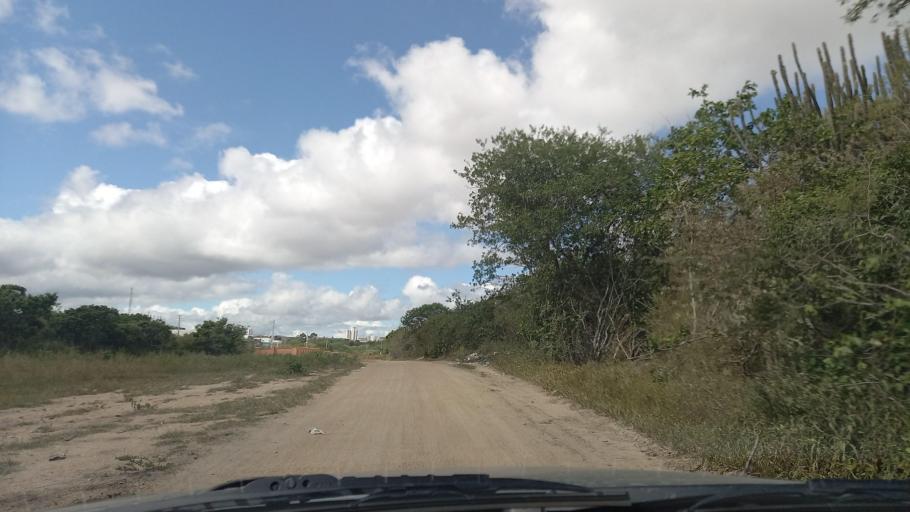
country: BR
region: Pernambuco
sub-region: Caruaru
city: Caruaru
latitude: -8.2469
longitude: -35.9825
